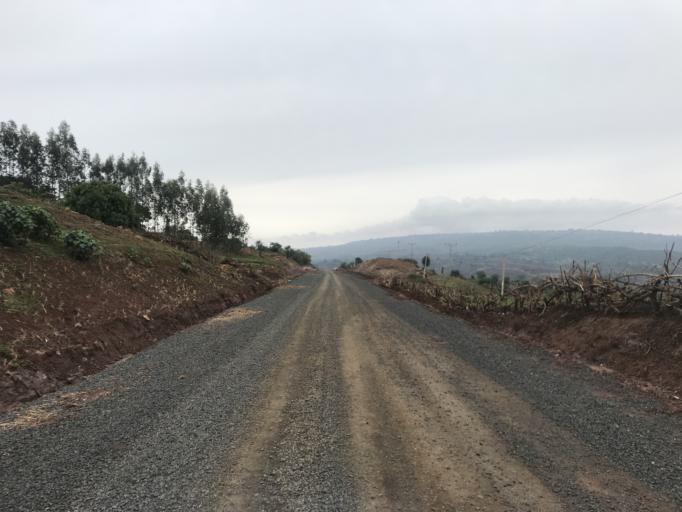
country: ET
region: Oromiya
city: Shambu
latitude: 10.0740
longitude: 36.8792
